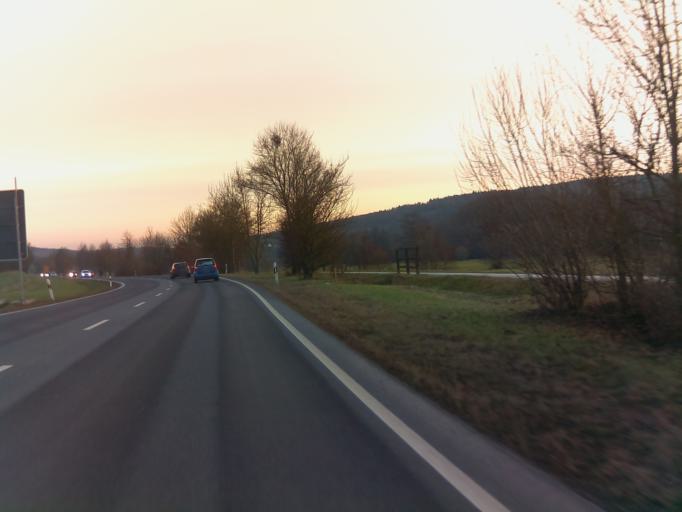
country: DE
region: Bavaria
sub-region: Regierungsbezirk Unterfranken
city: Oberelsbach
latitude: 50.3928
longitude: 10.0927
